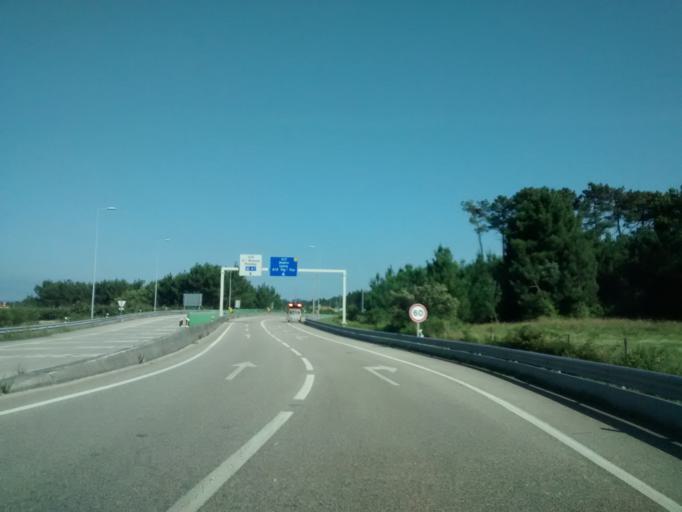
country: PT
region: Leiria
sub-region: Pombal
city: Lourical
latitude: 39.9909
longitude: -8.7897
